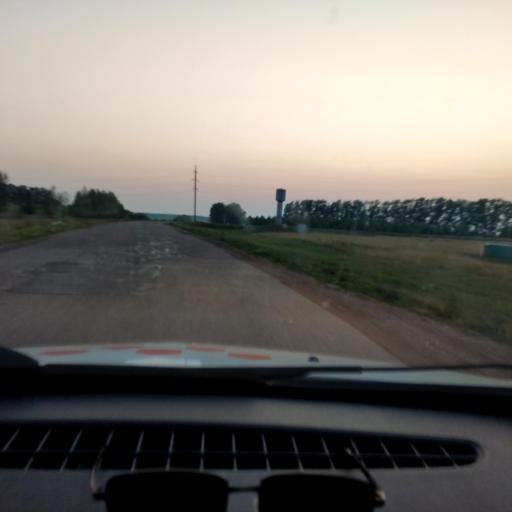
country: RU
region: Bashkortostan
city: Ulukulevo
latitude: 54.3695
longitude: 56.4273
